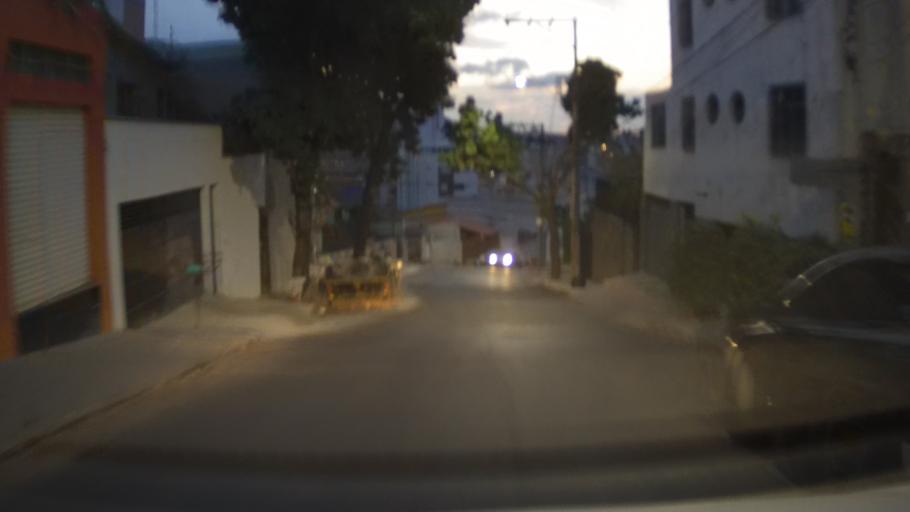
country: BR
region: Minas Gerais
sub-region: Belo Horizonte
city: Belo Horizonte
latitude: -19.8961
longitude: -43.9323
